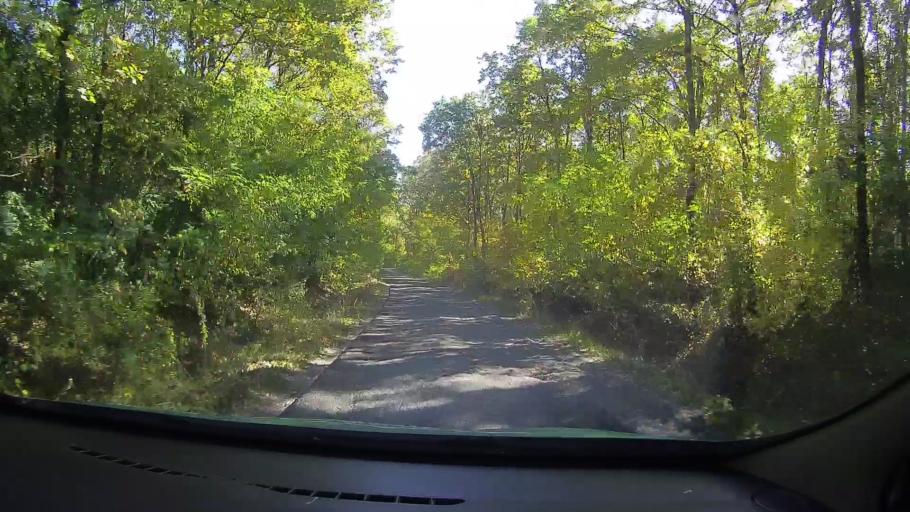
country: RO
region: Satu Mare
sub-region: Comuna Doba
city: Doba
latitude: 47.7168
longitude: 22.7418
